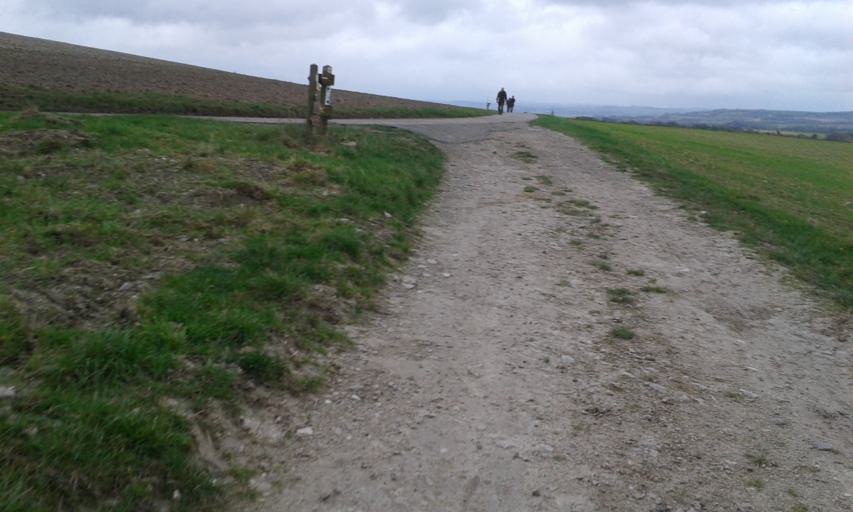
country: FR
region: Nord-Pas-de-Calais
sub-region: Departement du Pas-de-Calais
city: Wissant
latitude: 50.8742
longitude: 1.6982
